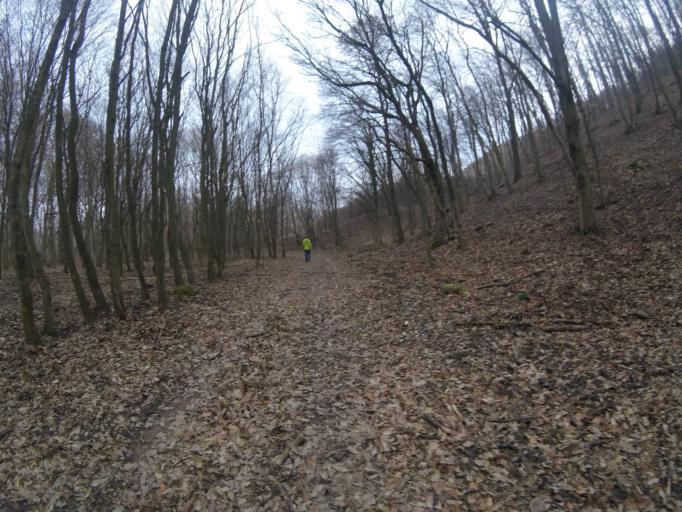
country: HU
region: Baranya
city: Mecseknadasd
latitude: 46.1474
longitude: 18.5155
